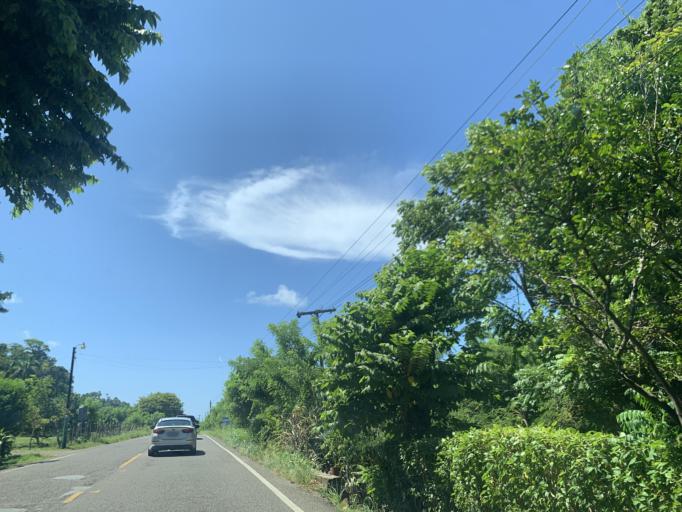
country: DO
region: Maria Trinidad Sanchez
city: Cabrera
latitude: 19.6646
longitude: -69.9437
